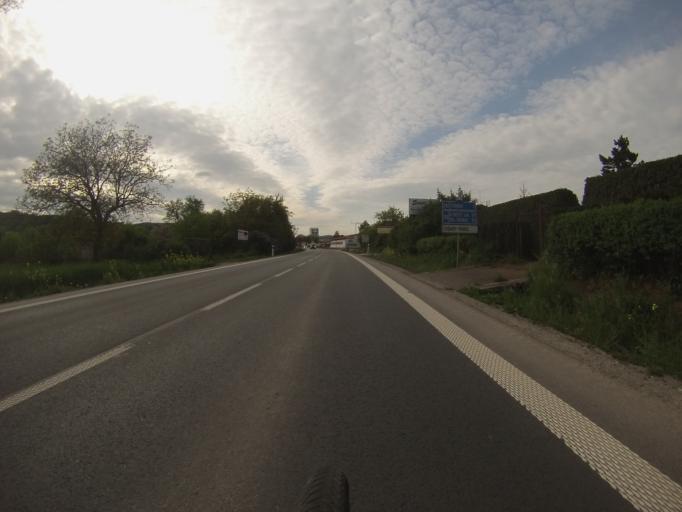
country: CZ
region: South Moravian
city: Tisnov
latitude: 49.3353
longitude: 16.4358
